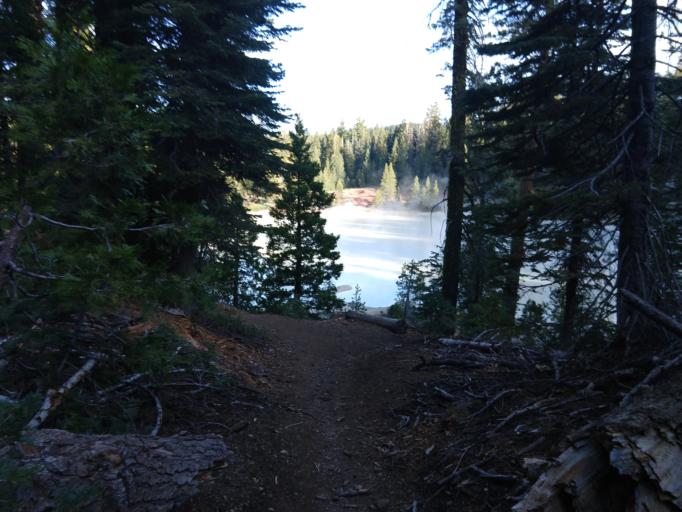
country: US
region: California
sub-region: Plumas County
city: Chester
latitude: 40.4346
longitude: -121.3973
